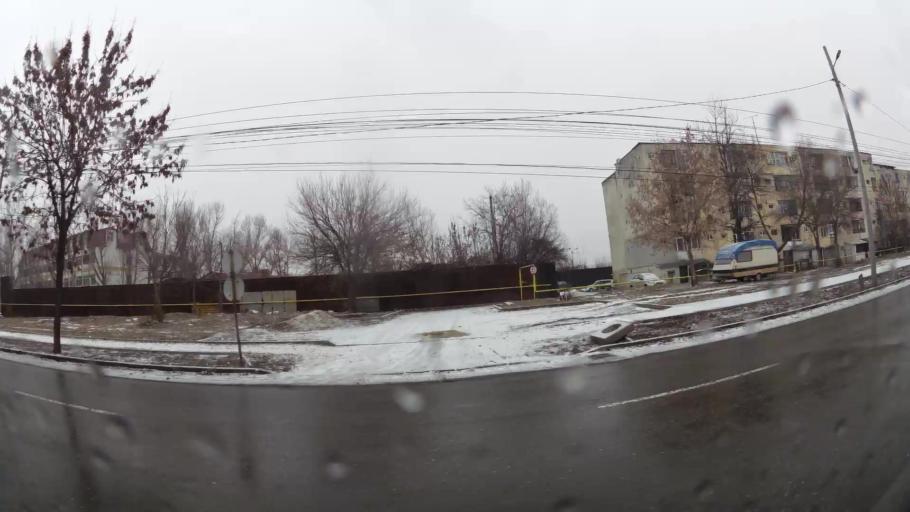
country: RO
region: Dambovita
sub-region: Municipiul Targoviste
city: Targoviste
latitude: 44.9120
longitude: 25.4469
